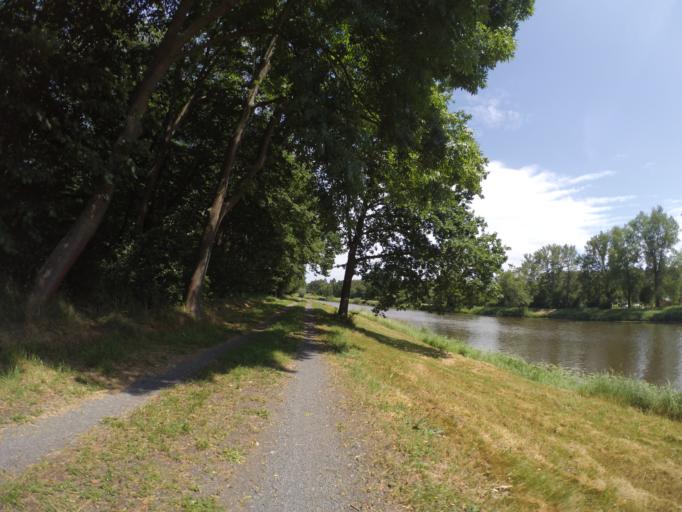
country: CZ
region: Central Bohemia
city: Poricany
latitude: 50.1658
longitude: 14.9126
